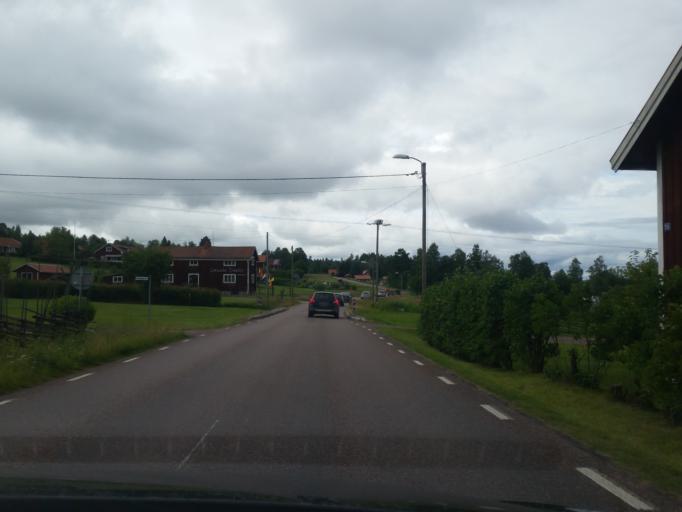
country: SE
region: Dalarna
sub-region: Leksand Municipality
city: Leksand
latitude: 60.7278
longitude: 14.9523
